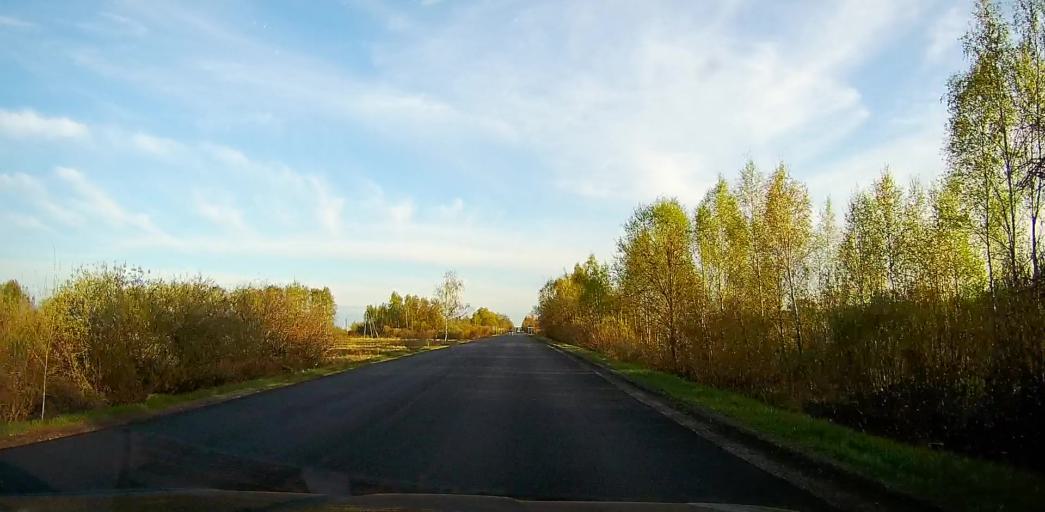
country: RU
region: Moskovskaya
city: Bronnitsy
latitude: 55.2805
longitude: 38.2178
